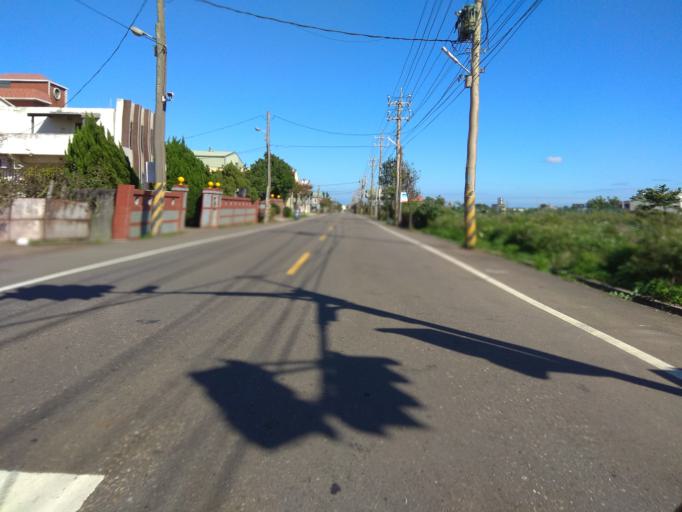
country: TW
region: Taiwan
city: Taoyuan City
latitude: 24.9949
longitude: 121.1355
